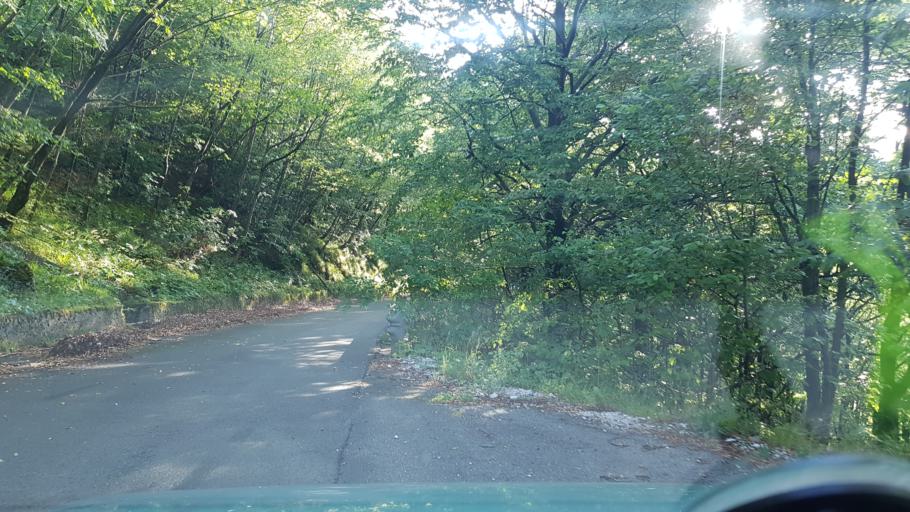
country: IT
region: Friuli Venezia Giulia
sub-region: Provincia di Udine
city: Lusevera
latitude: 46.3105
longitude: 13.2640
